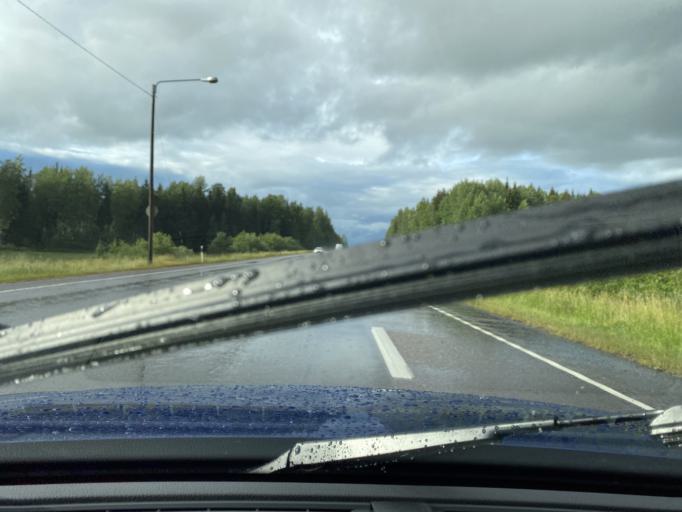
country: FI
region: Uusimaa
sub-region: Helsinki
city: Nurmijaervi
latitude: 60.4613
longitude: 24.8337
